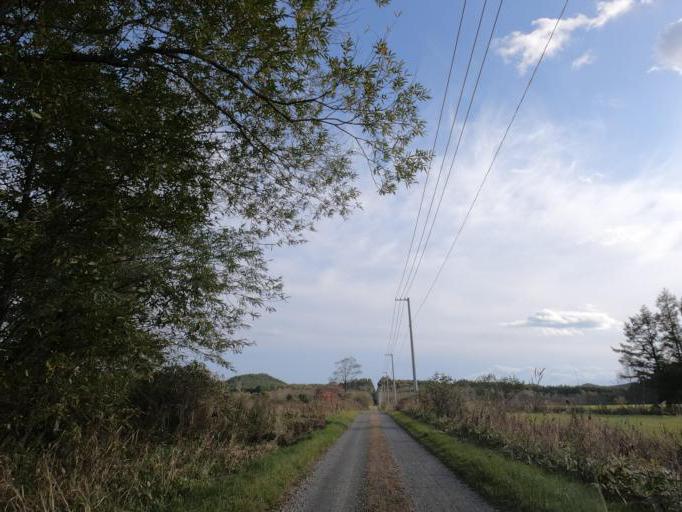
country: JP
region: Hokkaido
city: Obihiro
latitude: 42.5390
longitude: 143.3659
